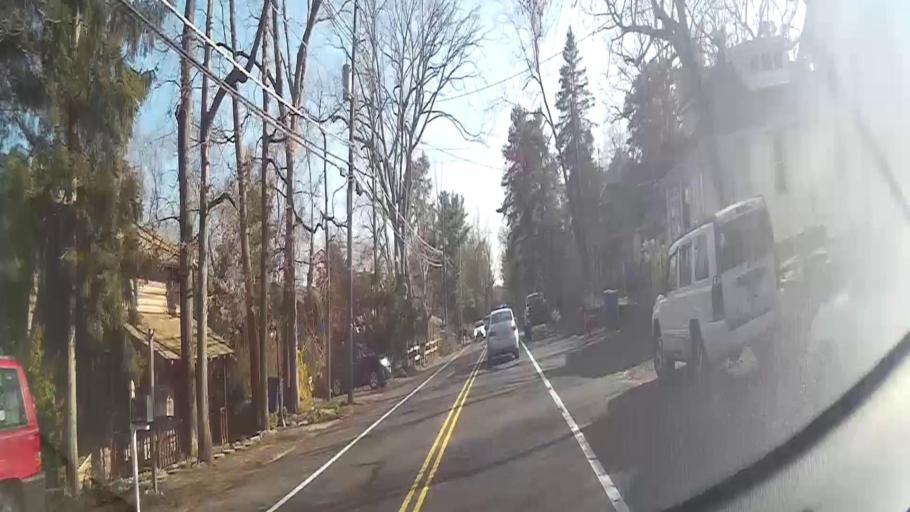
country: US
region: New Jersey
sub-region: Burlington County
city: Medford Lakes
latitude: 39.8616
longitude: -74.8531
